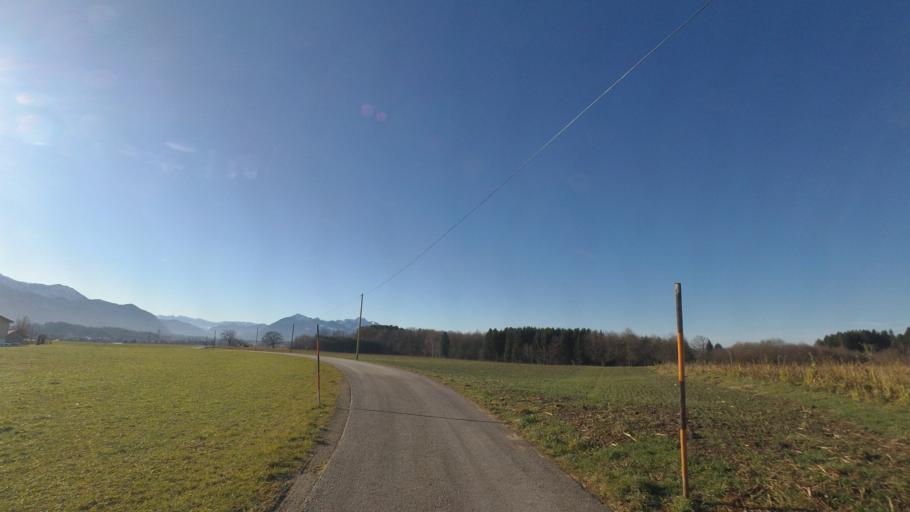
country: DE
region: Bavaria
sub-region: Upper Bavaria
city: Grabenstatt
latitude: 47.8583
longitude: 12.5519
